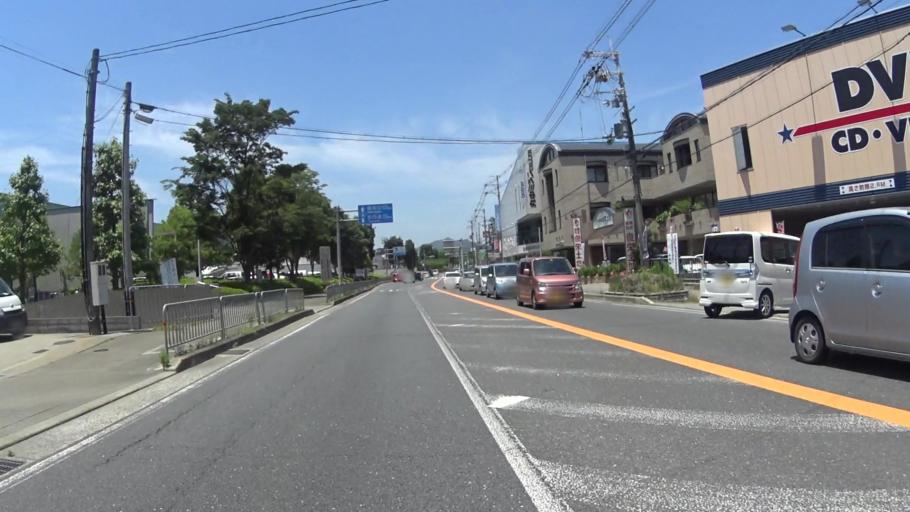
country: JP
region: Kyoto
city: Kameoka
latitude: 35.0147
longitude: 135.5688
